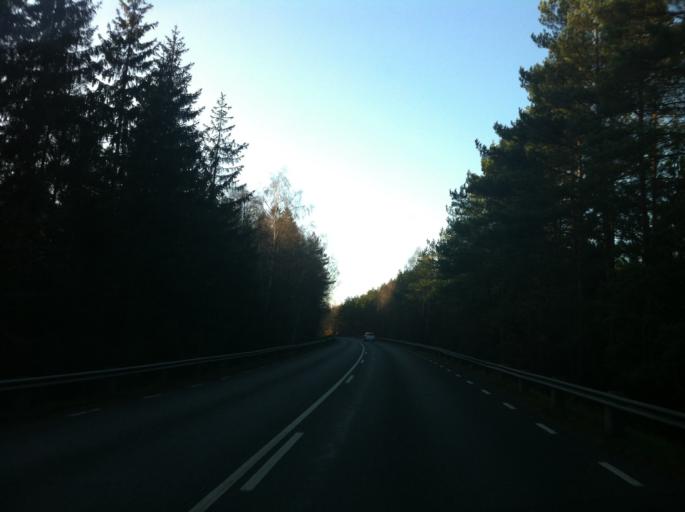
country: SE
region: Skane
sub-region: Kristianstads Kommun
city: Tollarp
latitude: 56.1846
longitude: 14.3307
